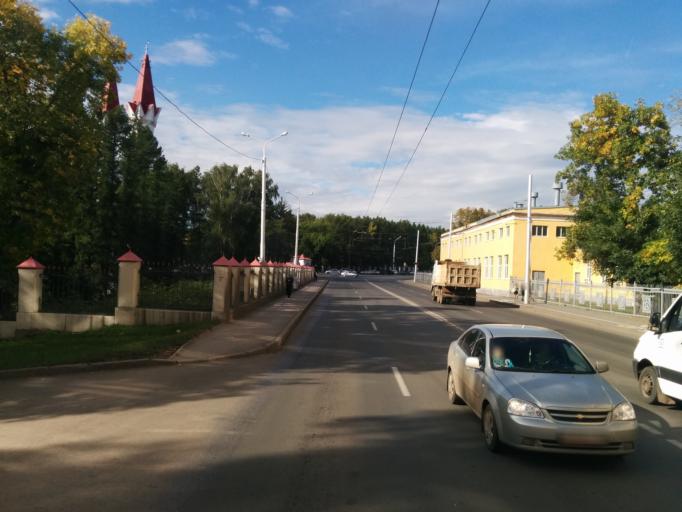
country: RU
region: Bashkortostan
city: Ufa
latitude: 54.8187
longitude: 56.0572
